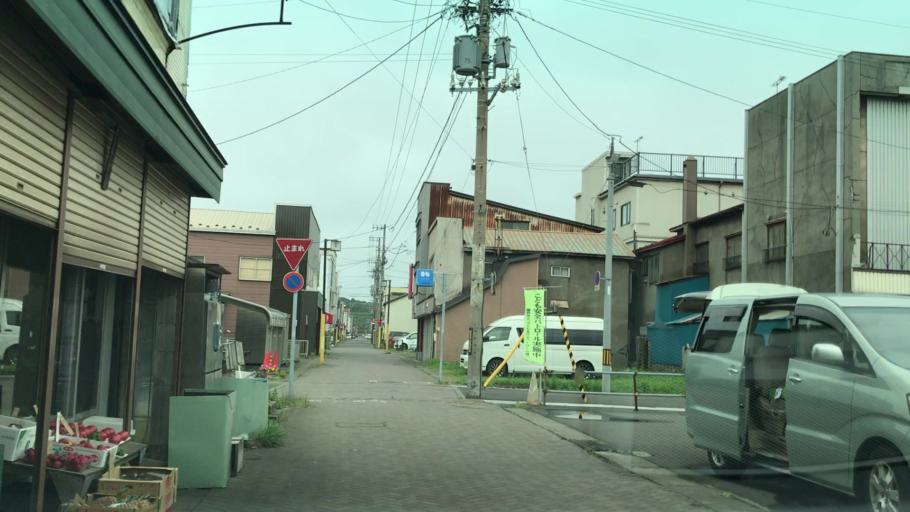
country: JP
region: Hokkaido
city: Muroran
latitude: 42.3334
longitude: 141.0089
